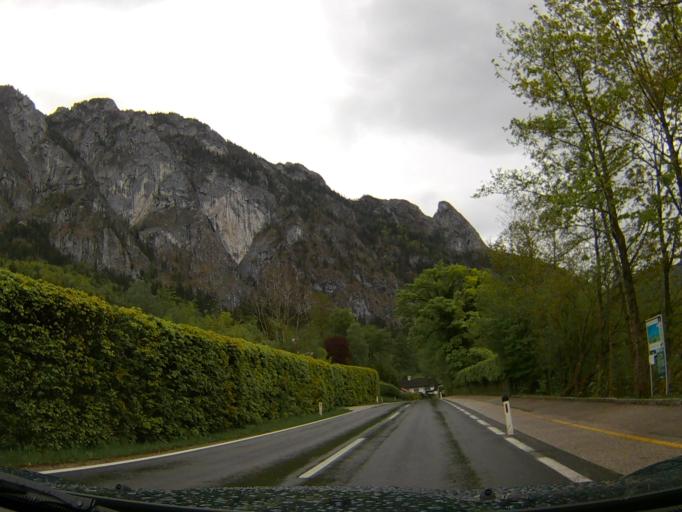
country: AT
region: Upper Austria
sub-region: Politischer Bezirk Vocklabruck
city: Steinbach am Attersee
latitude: 47.8129
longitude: 13.5468
